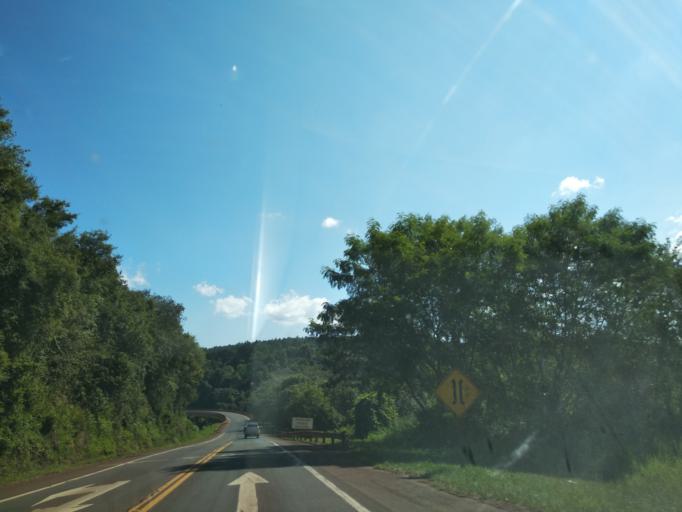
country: AR
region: Misiones
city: Puerto Piray
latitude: -26.4801
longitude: -54.6542
